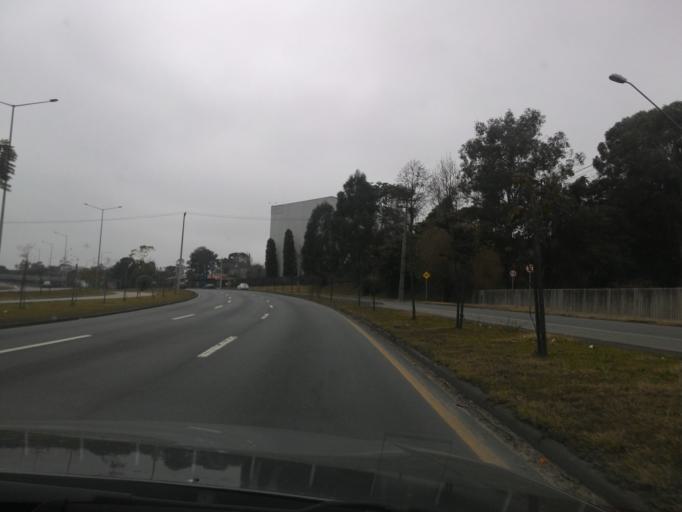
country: BR
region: Parana
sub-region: Curitiba
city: Curitiba
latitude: -25.4518
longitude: -49.2384
